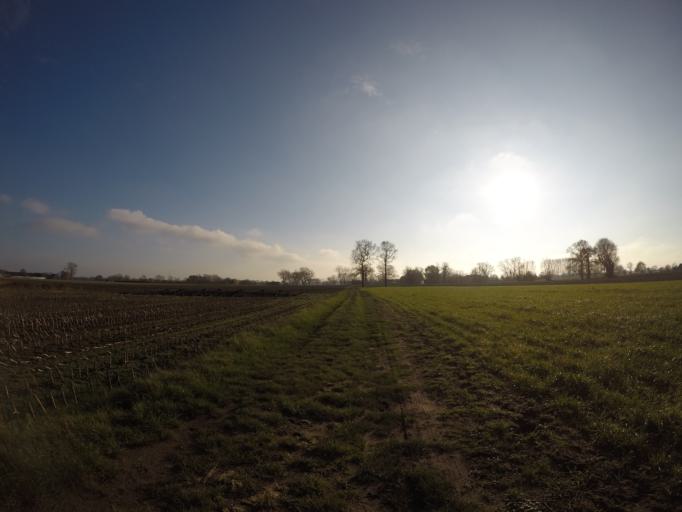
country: BE
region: Flanders
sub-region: Provincie West-Vlaanderen
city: Lichtervelde
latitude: 51.0617
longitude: 3.1931
